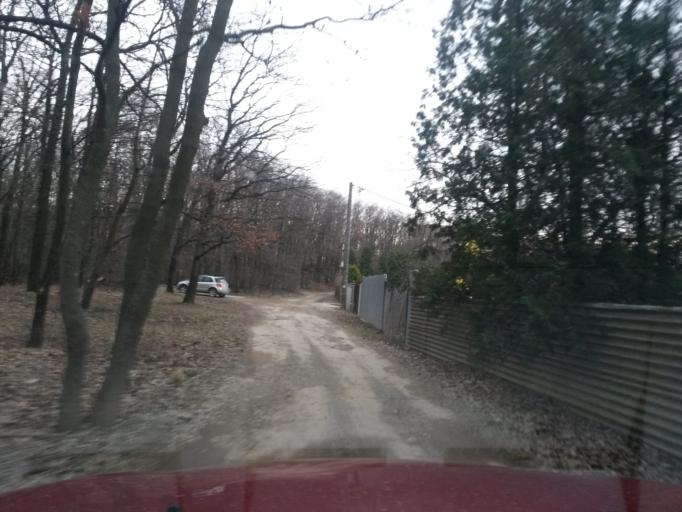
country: SK
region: Kosicky
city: Kosice
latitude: 48.7019
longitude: 21.2943
